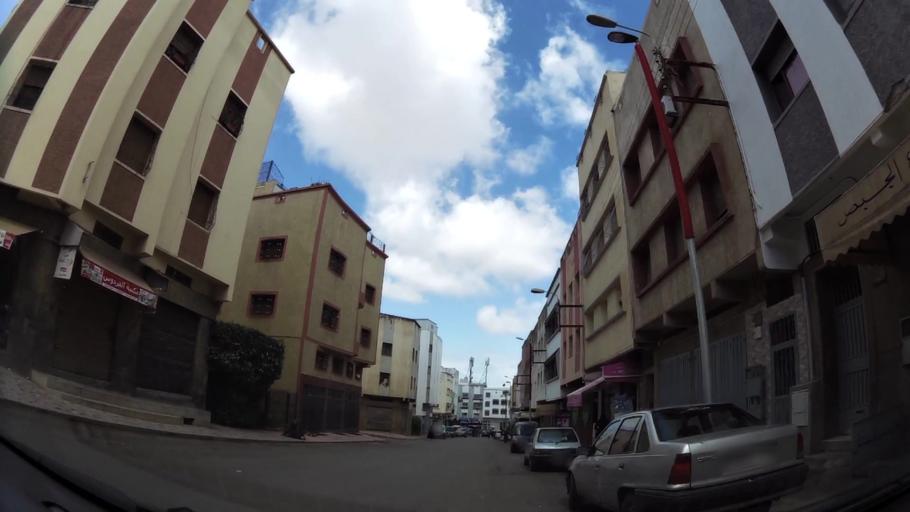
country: MA
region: Grand Casablanca
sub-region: Casablanca
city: Casablanca
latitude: 33.5364
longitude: -7.5852
